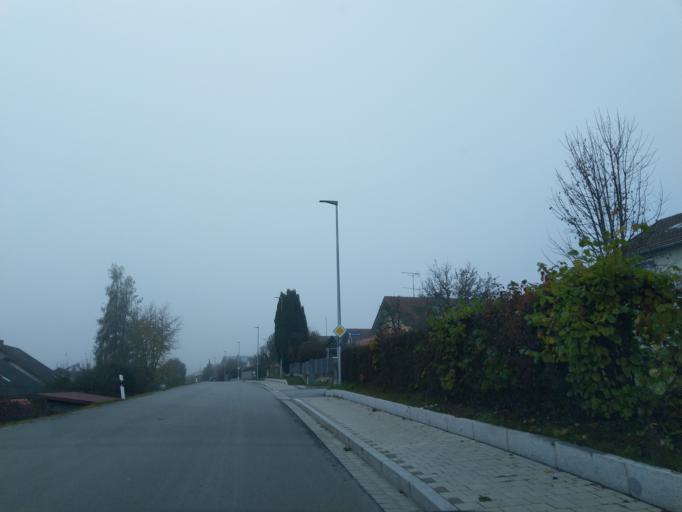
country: DE
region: Bavaria
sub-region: Lower Bavaria
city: Hengersberg
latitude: 48.7722
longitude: 13.0631
